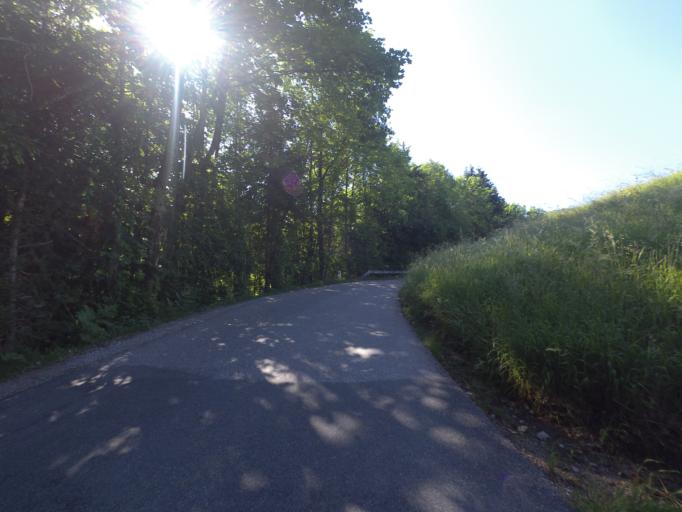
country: AT
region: Salzburg
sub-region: Politischer Bezirk Salzburg-Umgebung
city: Elsbethen
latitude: 47.7631
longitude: 13.1045
